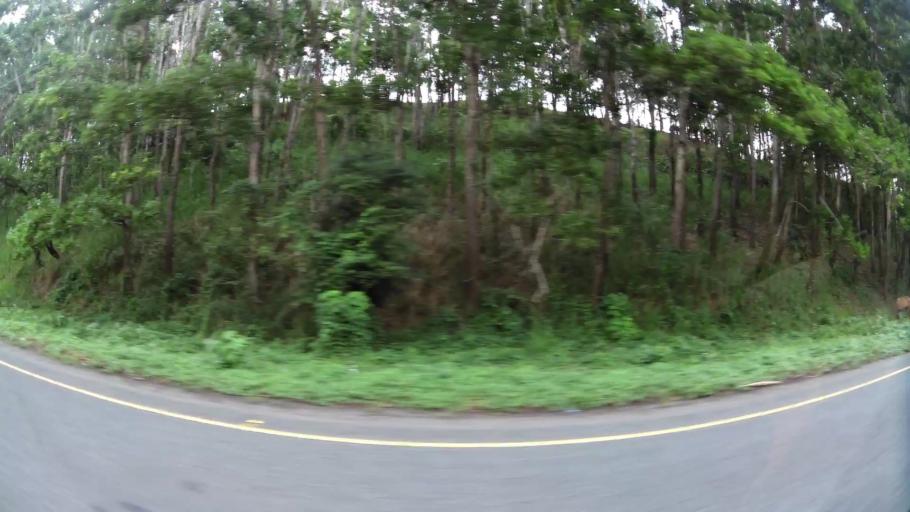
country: DO
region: Monsenor Nouel
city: Piedra Blanca
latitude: 18.8204
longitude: -70.2894
